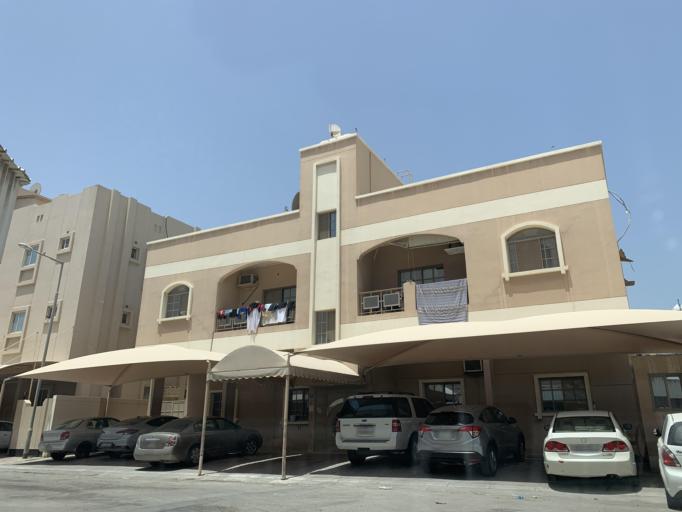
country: BH
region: Northern
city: Sitrah
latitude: 26.1412
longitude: 50.5890
